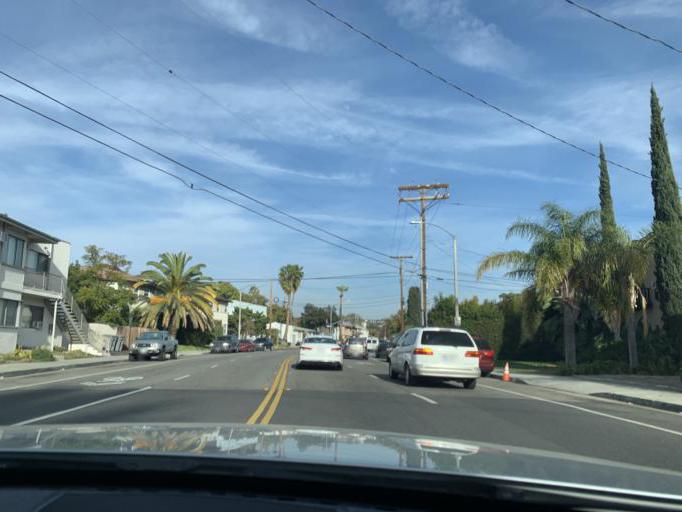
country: US
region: California
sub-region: Los Angeles County
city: Glendale
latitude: 34.1335
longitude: -118.2505
